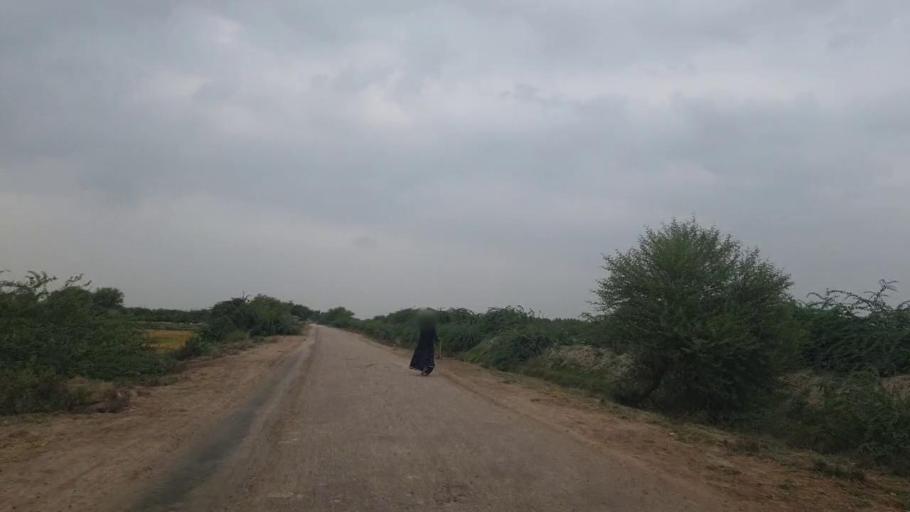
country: PK
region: Sindh
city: Badin
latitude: 24.6364
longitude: 68.6820
